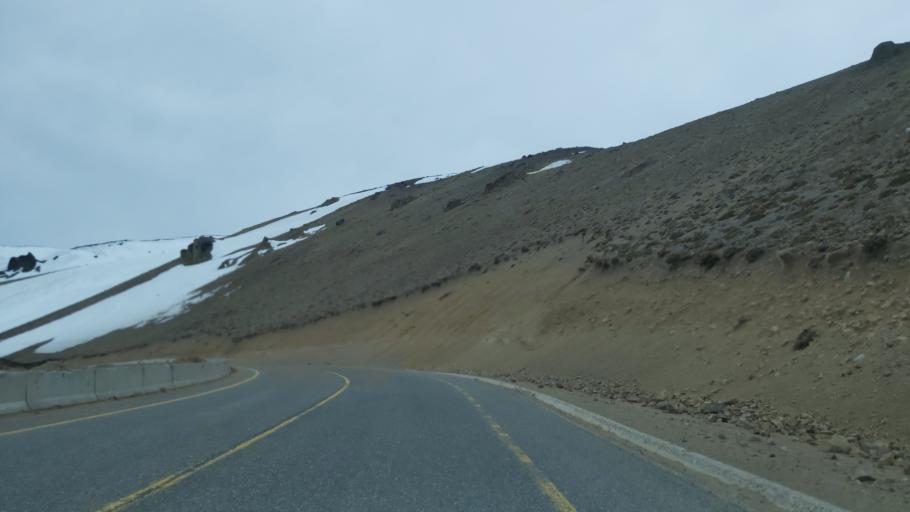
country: CL
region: Maule
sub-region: Provincia de Linares
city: Colbun
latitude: -36.0211
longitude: -70.5034
